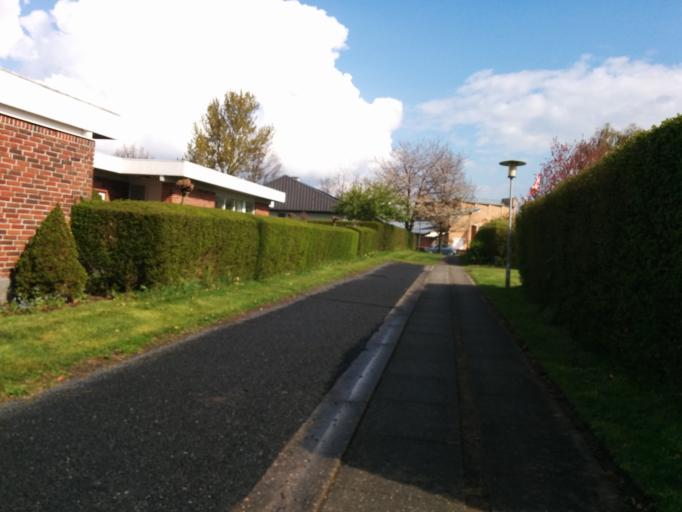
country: DK
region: Central Jutland
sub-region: Arhus Kommune
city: Hjortshoj
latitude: 56.2330
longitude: 10.3041
